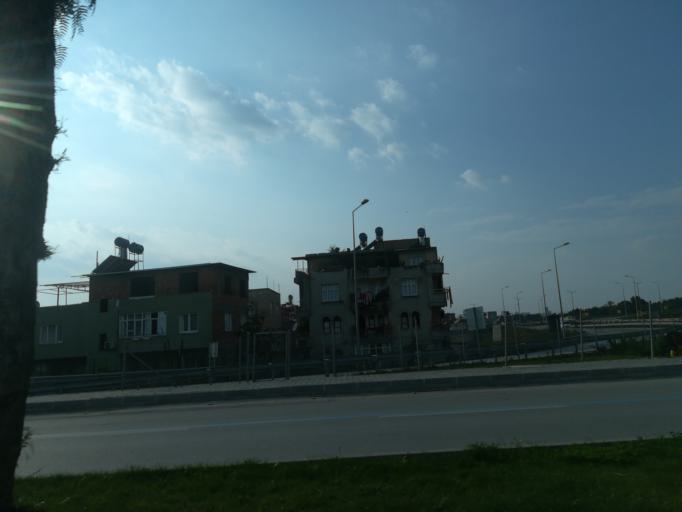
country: TR
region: Adana
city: Adana
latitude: 37.0213
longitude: 35.3424
